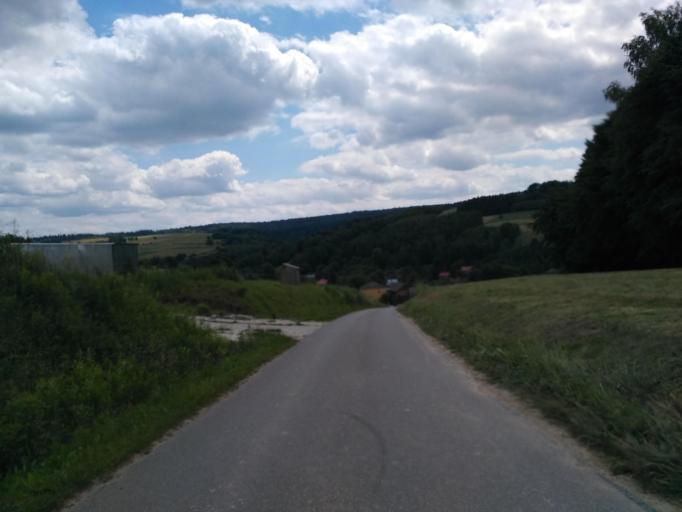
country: PL
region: Subcarpathian Voivodeship
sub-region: Powiat brzozowski
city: Nozdrzec
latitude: 49.7623
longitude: 22.1884
